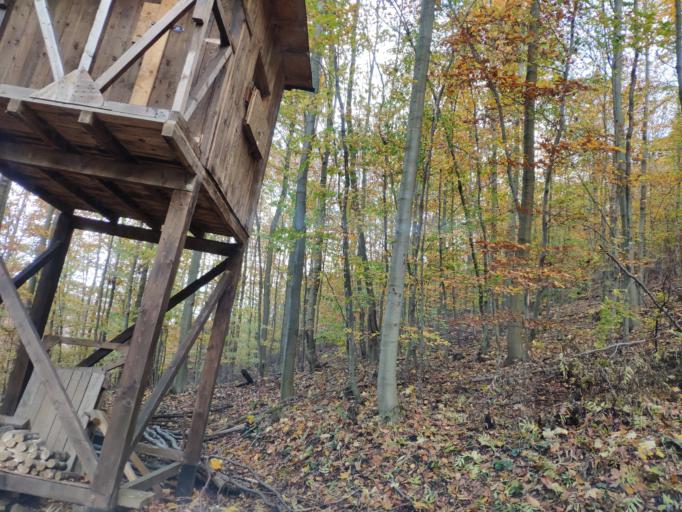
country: SK
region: Presovsky
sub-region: Okres Presov
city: Presov
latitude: 48.8549
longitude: 21.1894
